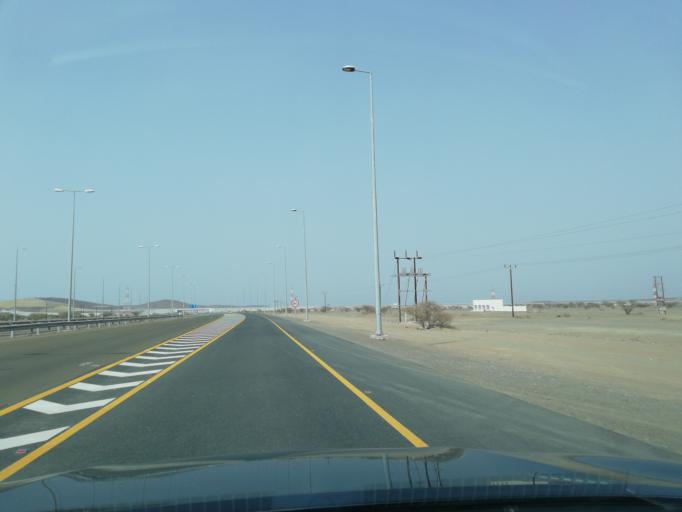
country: OM
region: Al Batinah
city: Al Liwa'
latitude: 24.3776
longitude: 56.5412
